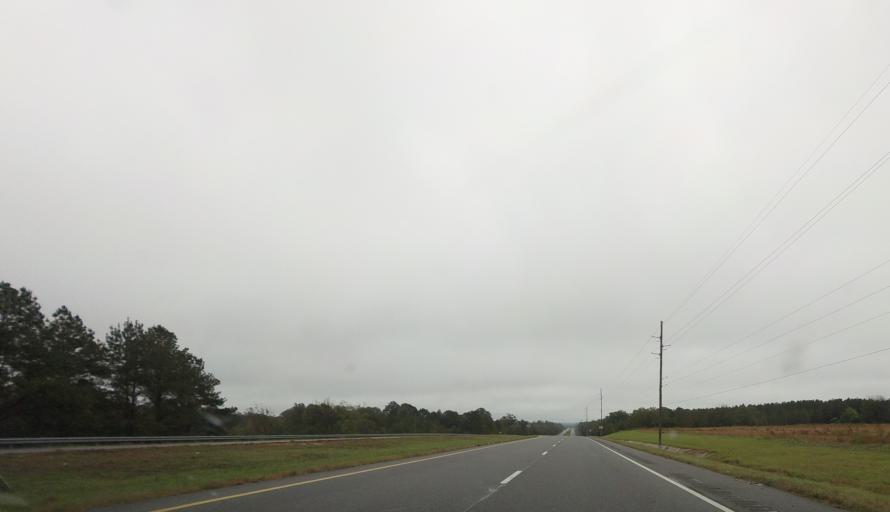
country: US
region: Georgia
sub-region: Taylor County
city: Reynolds
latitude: 32.5556
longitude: -84.0600
